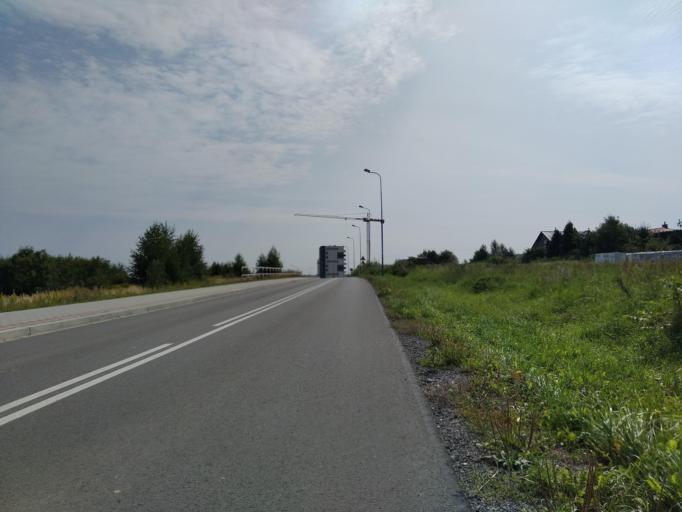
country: PL
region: Subcarpathian Voivodeship
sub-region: Powiat ropczycko-sedziszowski
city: Ropczyce
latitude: 50.0648
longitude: 21.6061
